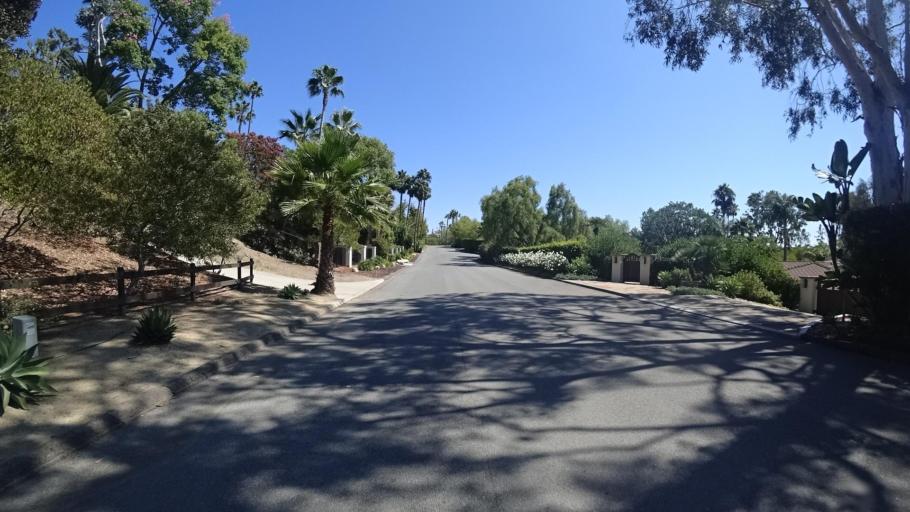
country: US
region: California
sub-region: San Diego County
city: Rancho Santa Fe
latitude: 33.0310
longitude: -117.1752
